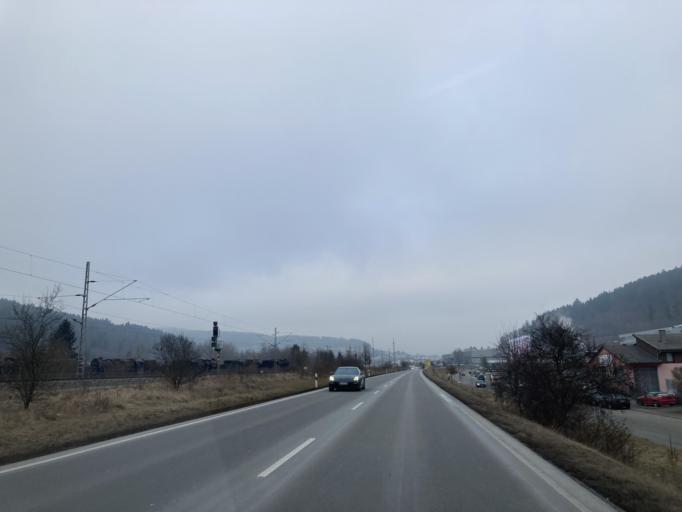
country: DE
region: Baden-Wuerttemberg
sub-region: Freiburg Region
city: Wurmlingen
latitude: 47.9715
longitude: 8.7896
